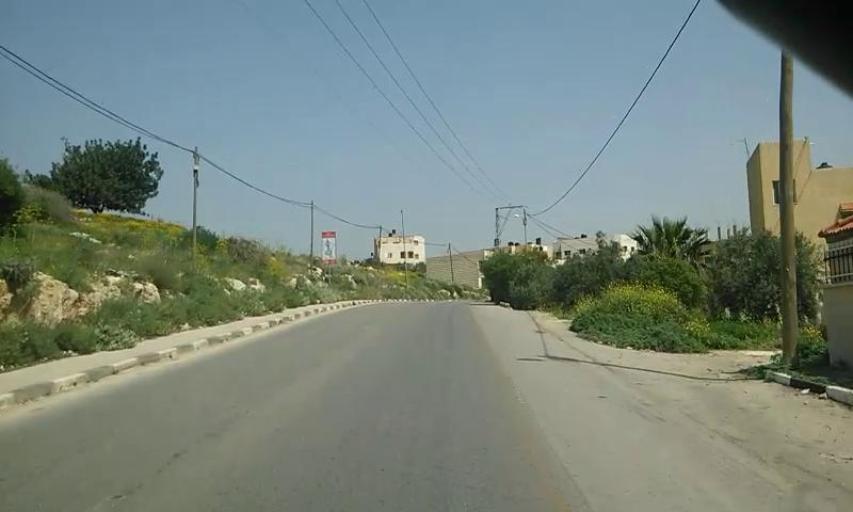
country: PS
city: Al Badhan
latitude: 32.2611
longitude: 35.3270
